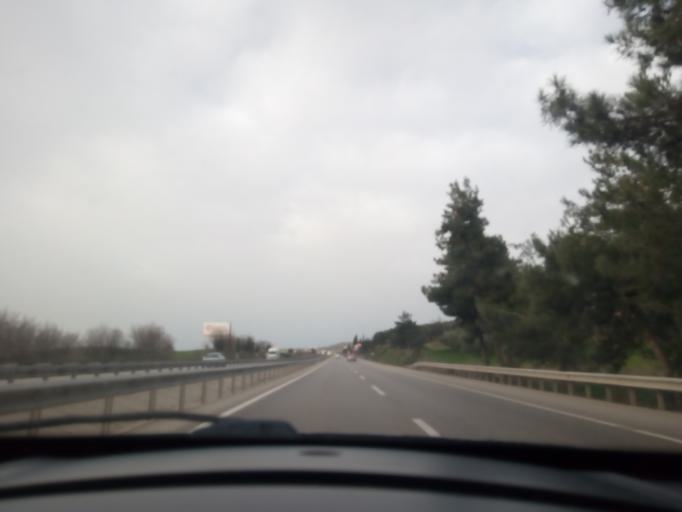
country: TR
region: Bursa
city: Gorukle
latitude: 40.2145
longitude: 28.7298
